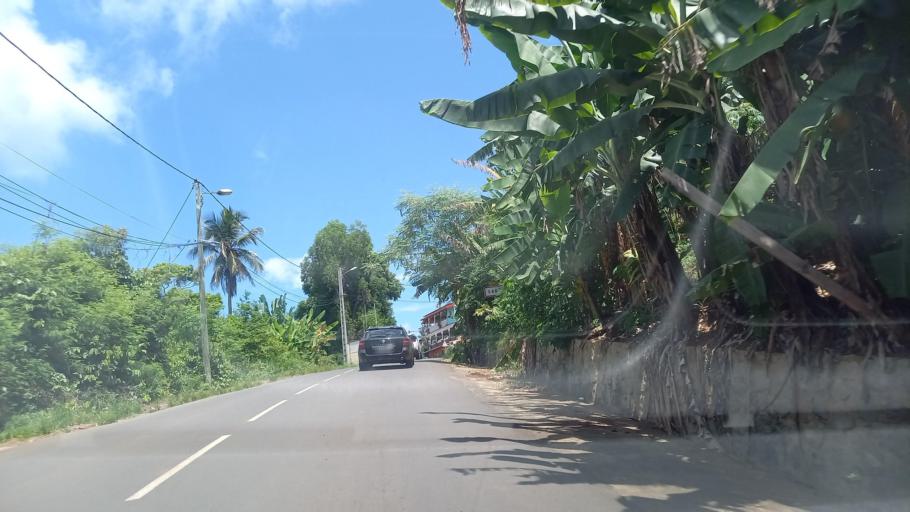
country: YT
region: Sada
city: Sada
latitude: -12.8562
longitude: 45.1003
